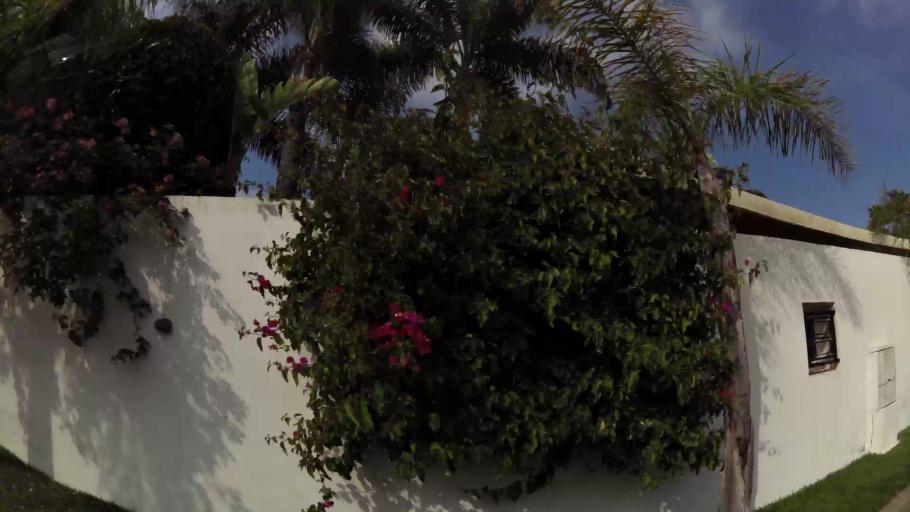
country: MA
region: Rabat-Sale-Zemmour-Zaer
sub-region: Rabat
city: Rabat
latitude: 33.9692
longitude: -6.8430
